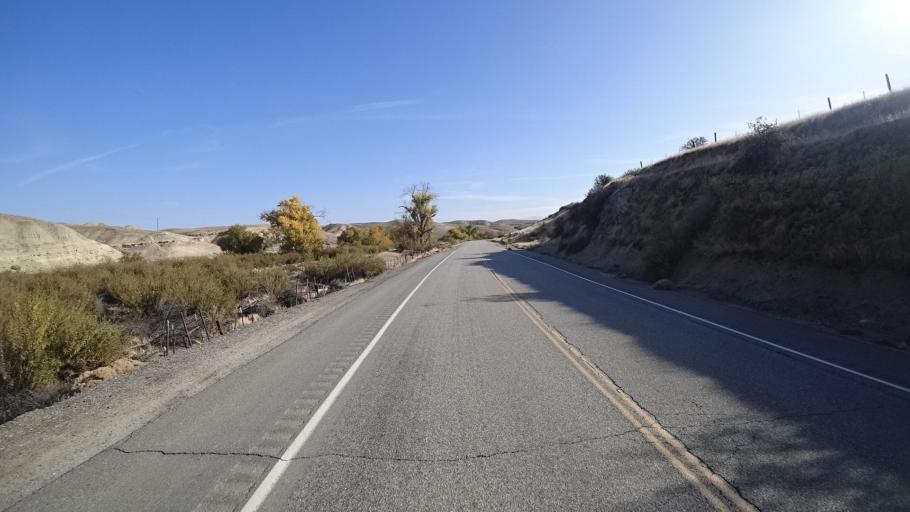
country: US
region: California
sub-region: Kern County
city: Oildale
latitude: 35.5289
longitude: -118.9669
